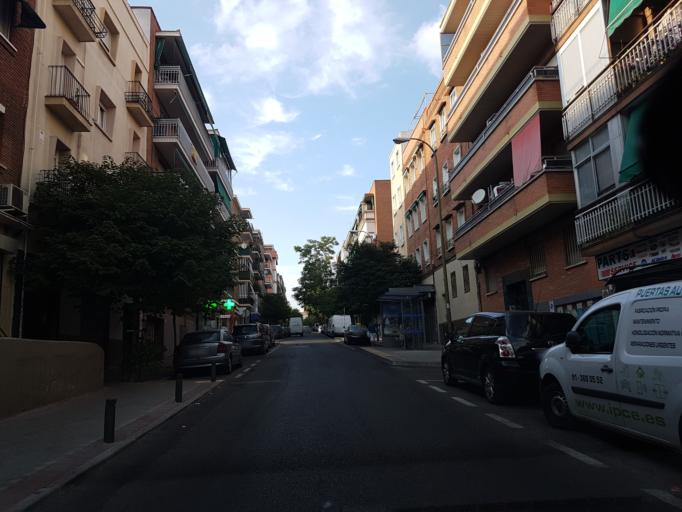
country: ES
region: Madrid
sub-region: Provincia de Madrid
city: Moratalaz
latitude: 40.4302
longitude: -3.6488
